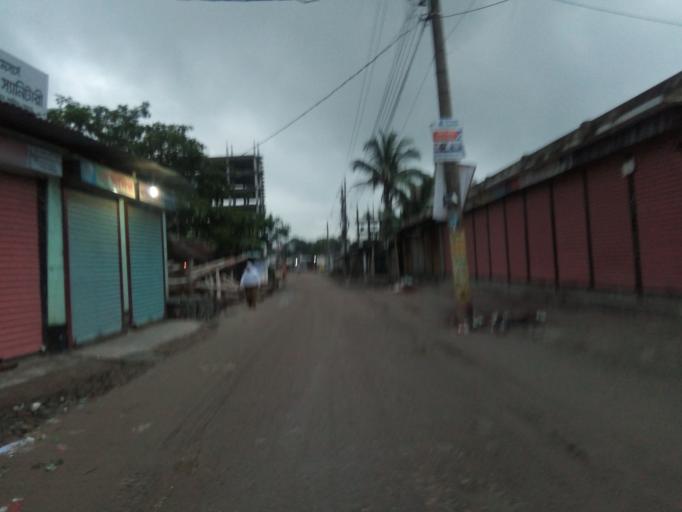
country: BD
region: Dhaka
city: Tungi
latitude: 23.8581
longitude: 90.4285
